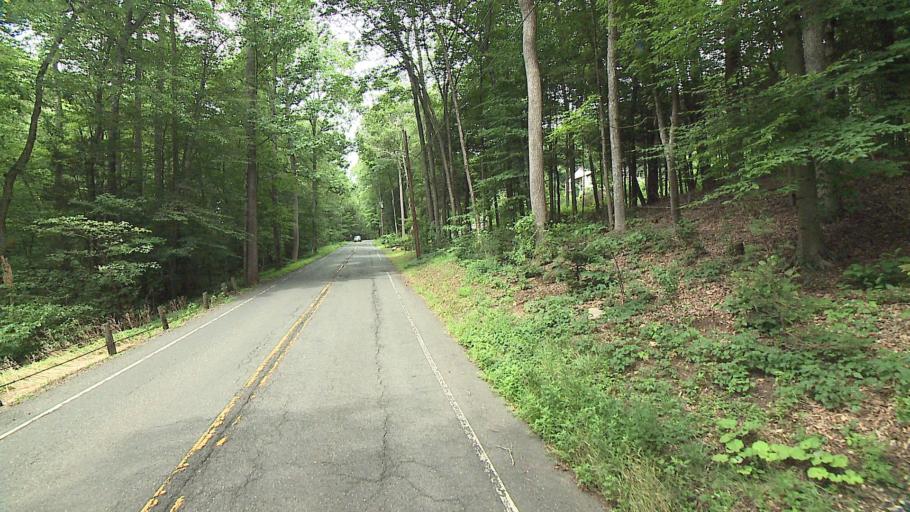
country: US
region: Connecticut
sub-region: Litchfield County
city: New Milford
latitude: 41.5035
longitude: -73.3587
